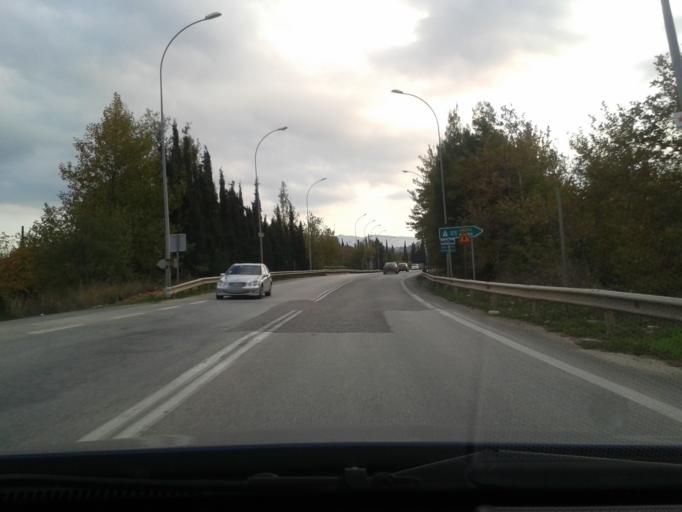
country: GR
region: Attica
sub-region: Nomarchia Anatolikis Attikis
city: Afidnes
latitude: 38.1898
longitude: 23.8545
